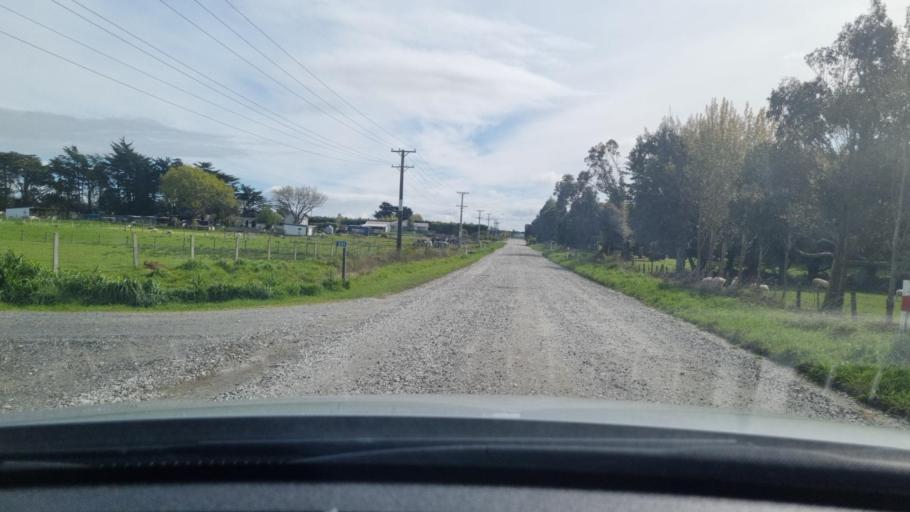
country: NZ
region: Southland
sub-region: Invercargill City
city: Invercargill
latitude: -46.4506
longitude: 168.3858
